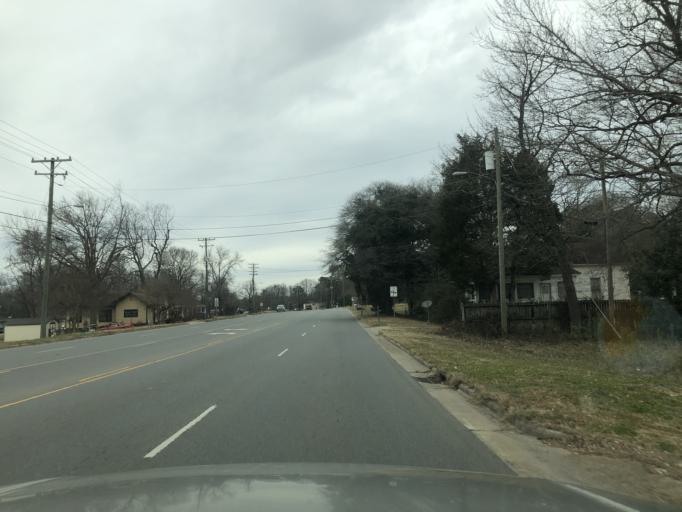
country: US
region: North Carolina
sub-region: Cleveland County
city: Shelby
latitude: 35.2849
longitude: -81.4913
